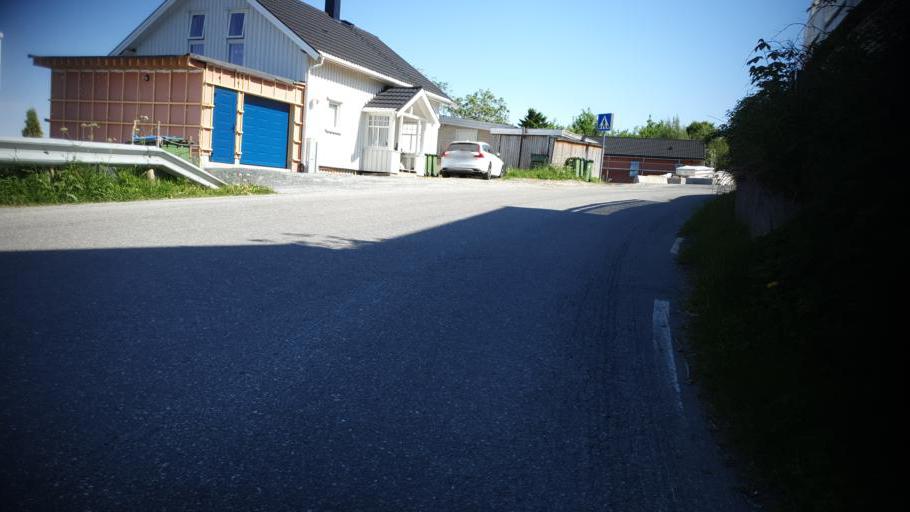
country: NO
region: Sor-Trondelag
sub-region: Malvik
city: Malvik
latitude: 63.4320
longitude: 10.6026
